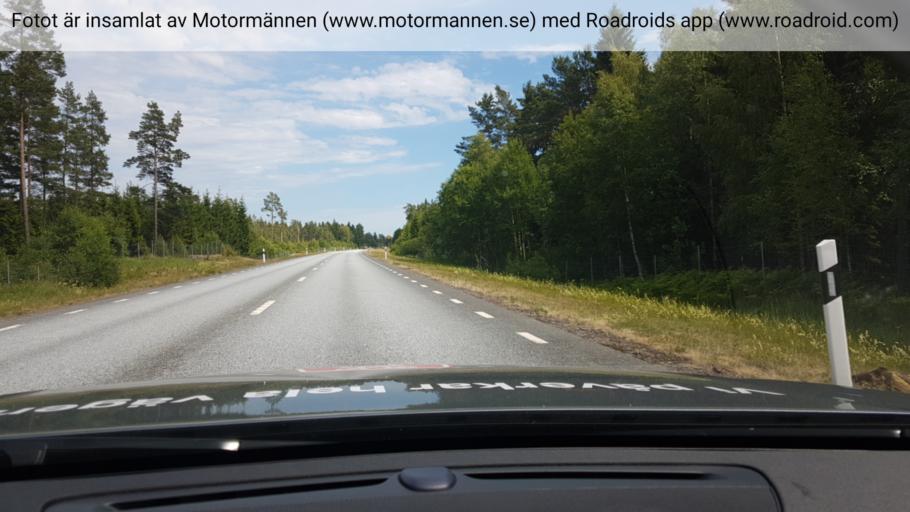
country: SE
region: Uppsala
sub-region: Osthammars Kommun
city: OEsthammar
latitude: 60.1731
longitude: 18.3427
